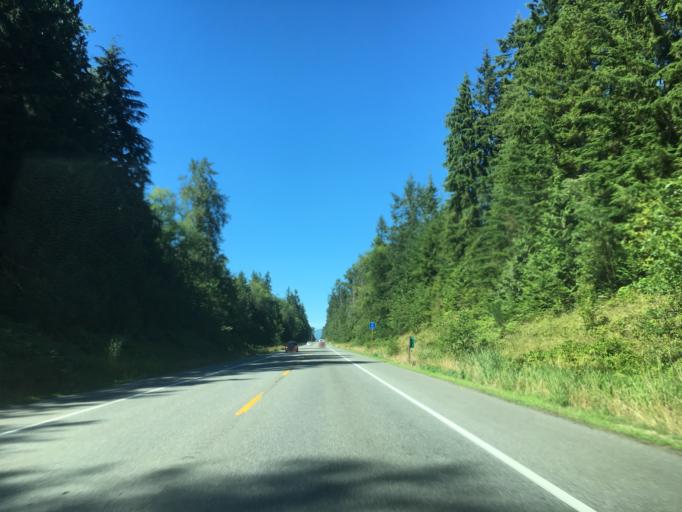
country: US
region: Washington
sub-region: Snohomish County
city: Sisco Heights
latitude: 48.1068
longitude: -122.1122
